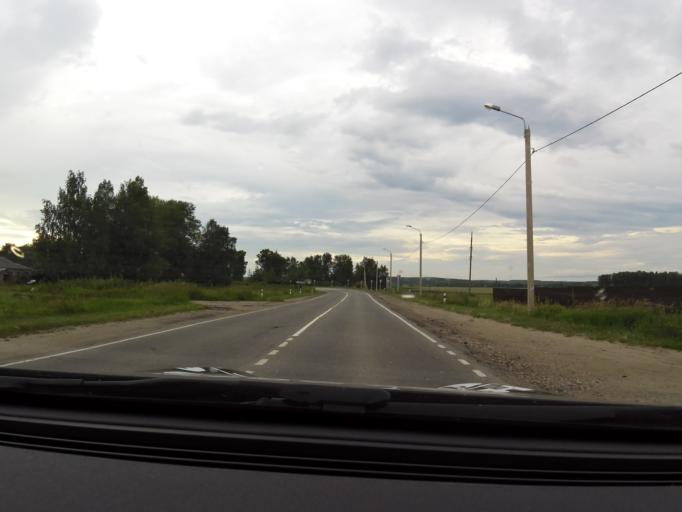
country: RU
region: Vladimir
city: Vorsha
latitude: 56.1060
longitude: 40.0768
